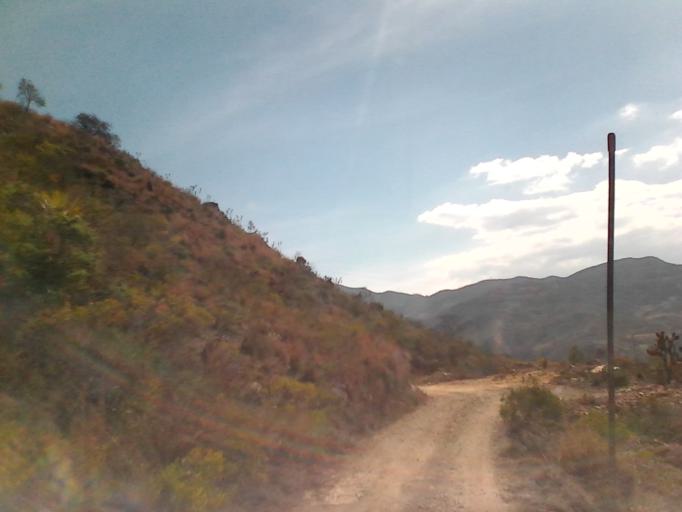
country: CO
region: Boyaca
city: Sachica
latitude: 5.5475
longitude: -73.5224
